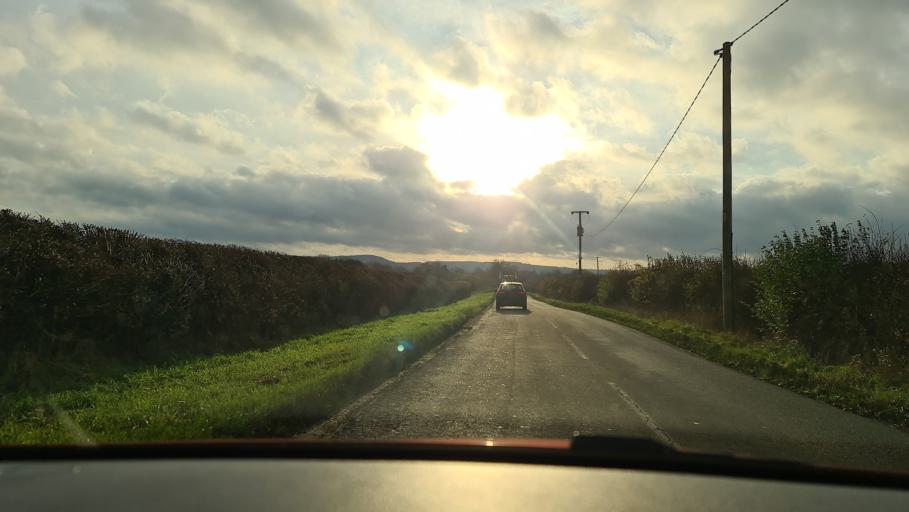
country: GB
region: England
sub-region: Buckinghamshire
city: Stone
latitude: 51.7824
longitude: -0.8805
